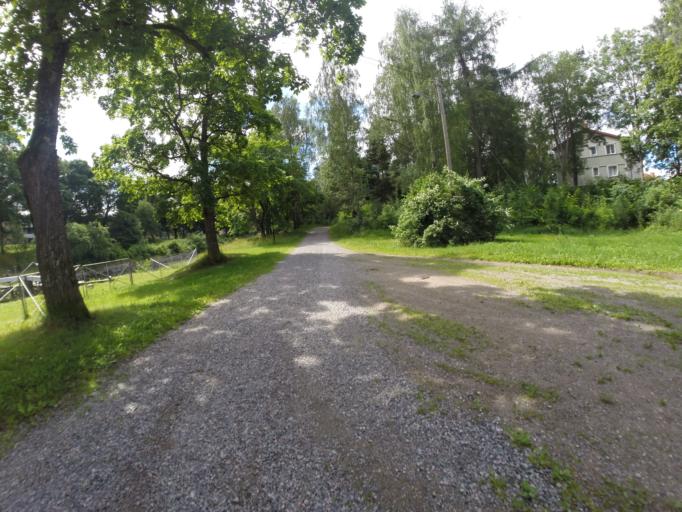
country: SE
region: Soedermanland
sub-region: Eskilstuna Kommun
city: Torshalla
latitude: 59.4226
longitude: 16.4822
